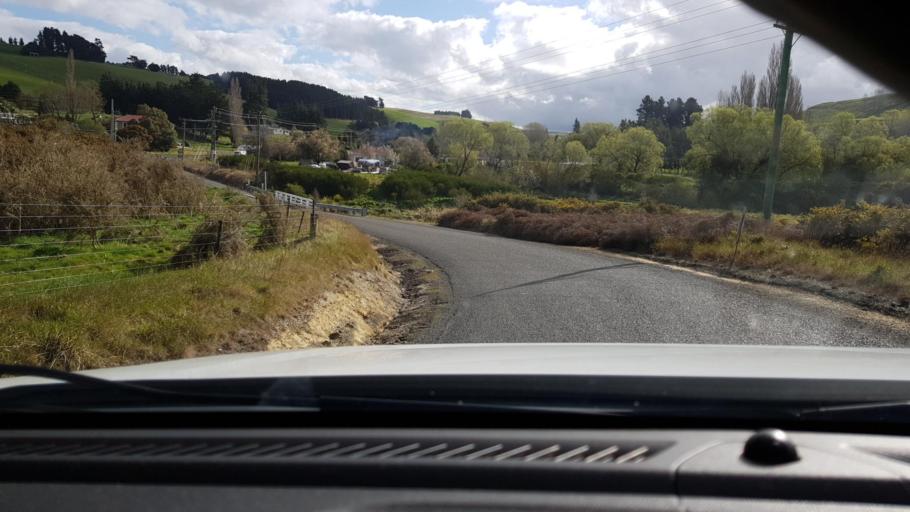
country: NZ
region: Otago
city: Oamaru
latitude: -44.9485
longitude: 170.7533
